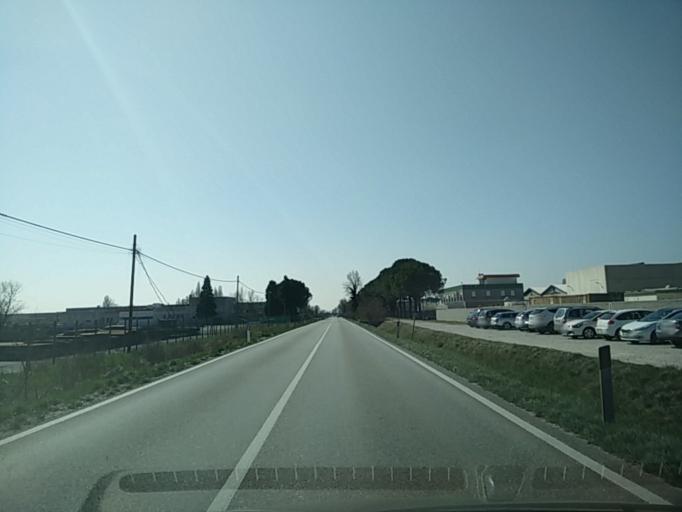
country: IT
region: Friuli Venezia Giulia
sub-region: Provincia di Udine
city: Sedegliano
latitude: 45.9905
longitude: 12.9314
